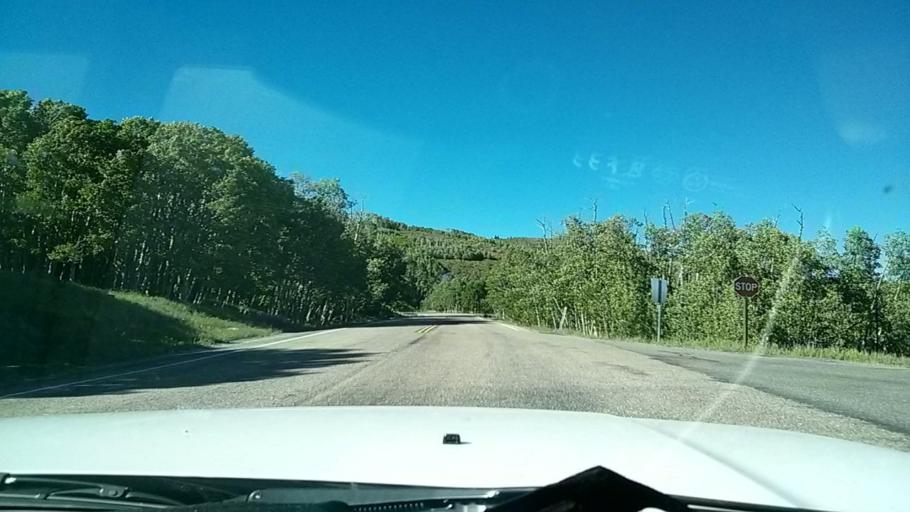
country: US
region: Utah
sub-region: Wayne County
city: Loa
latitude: 38.0276
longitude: -111.3432
